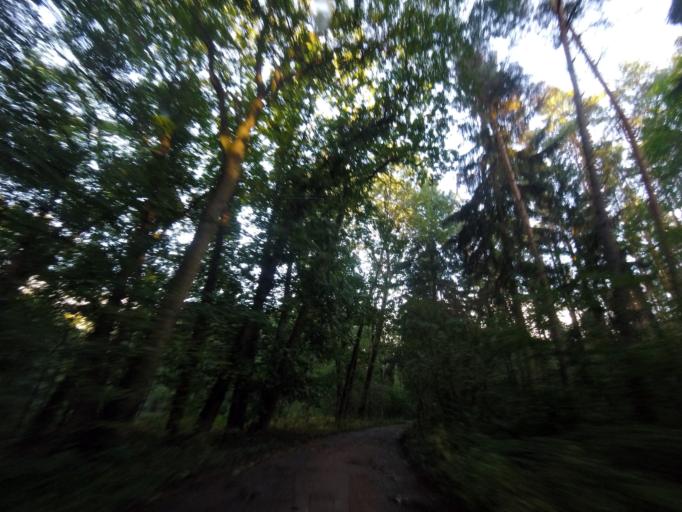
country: DE
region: Brandenburg
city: Treuenbrietzen
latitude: 52.0496
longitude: 12.8953
